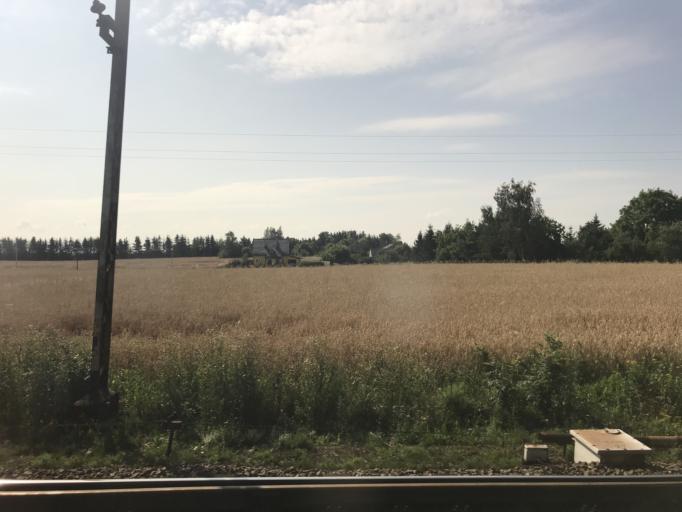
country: PL
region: Kujawsko-Pomorskie
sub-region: Powiat swiecki
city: Bukowiec
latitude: 53.3722
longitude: 18.2735
